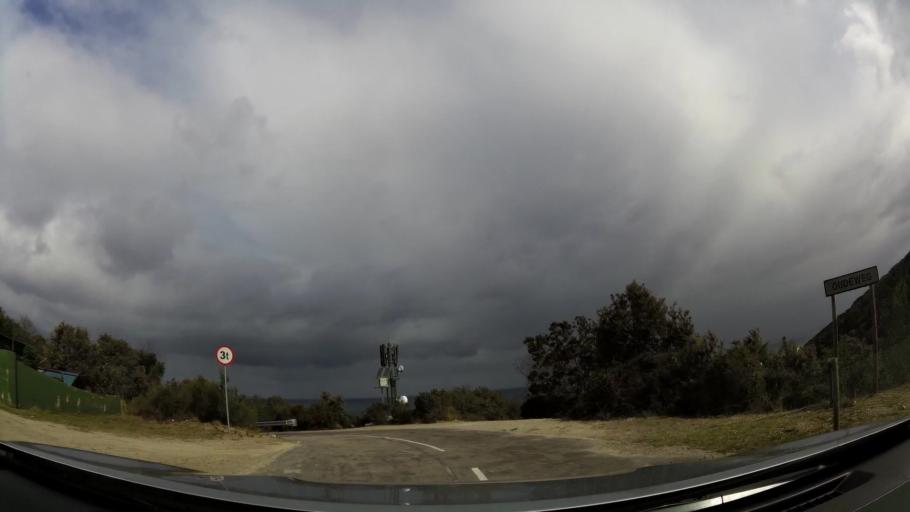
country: ZA
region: Western Cape
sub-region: Eden District Municipality
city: George
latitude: -34.0463
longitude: 22.3135
